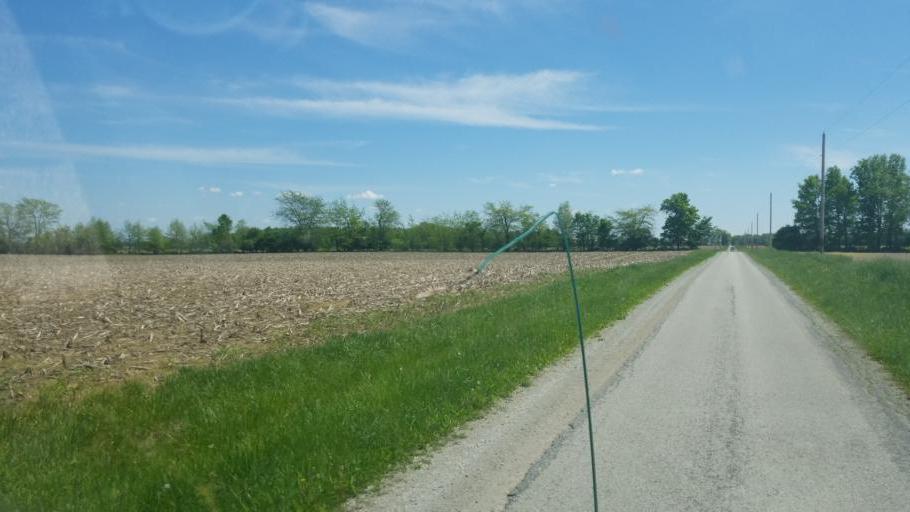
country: US
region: Ohio
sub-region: Sandusky County
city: Mount Carmel
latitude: 41.0607
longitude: -82.9390
